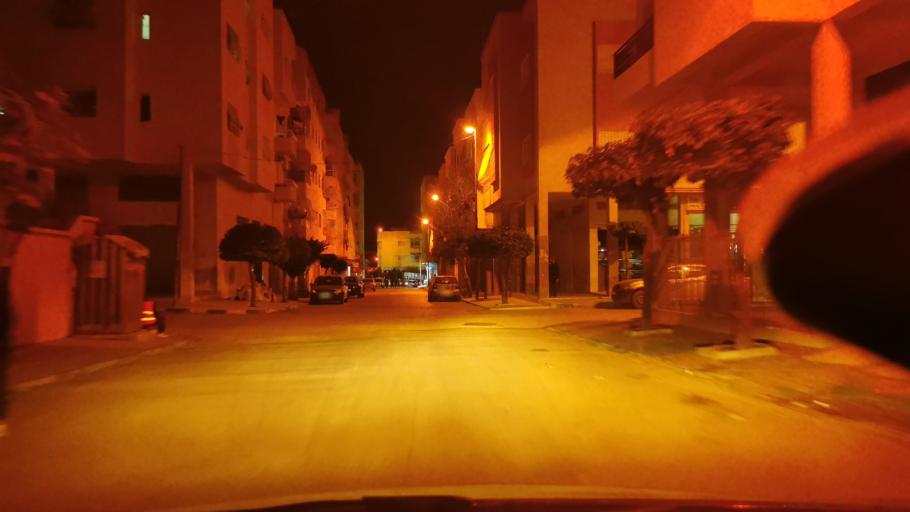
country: MA
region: Fes-Boulemane
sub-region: Fes
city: Fes
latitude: 34.0114
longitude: -4.9692
